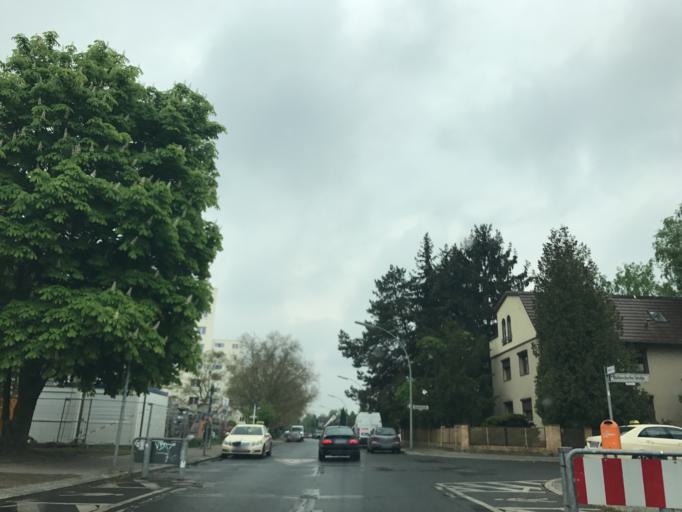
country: DE
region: Berlin
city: Falkenhagener Feld
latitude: 52.5465
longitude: 13.1770
